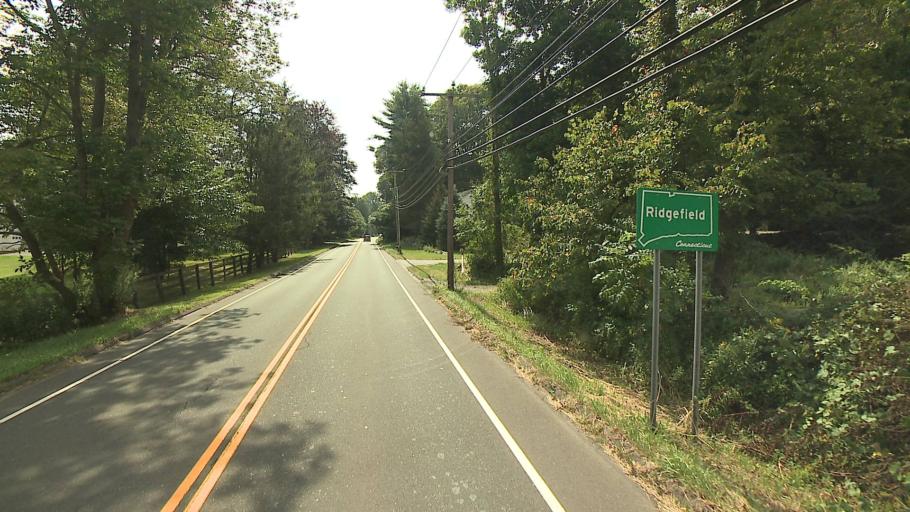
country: US
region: Connecticut
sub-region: Fairfield County
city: Ridgefield
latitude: 41.2965
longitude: -73.5047
